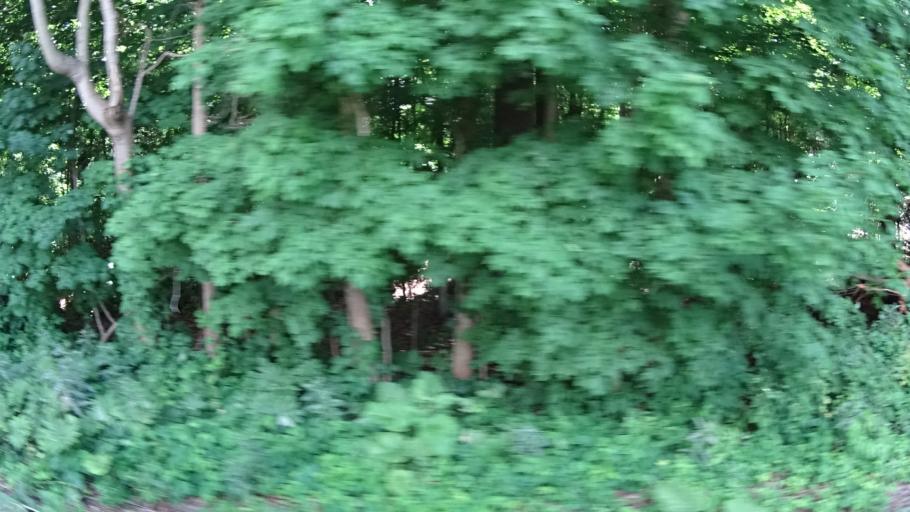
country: US
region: Ohio
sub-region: Erie County
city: Milan
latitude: 41.2920
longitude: -82.5970
